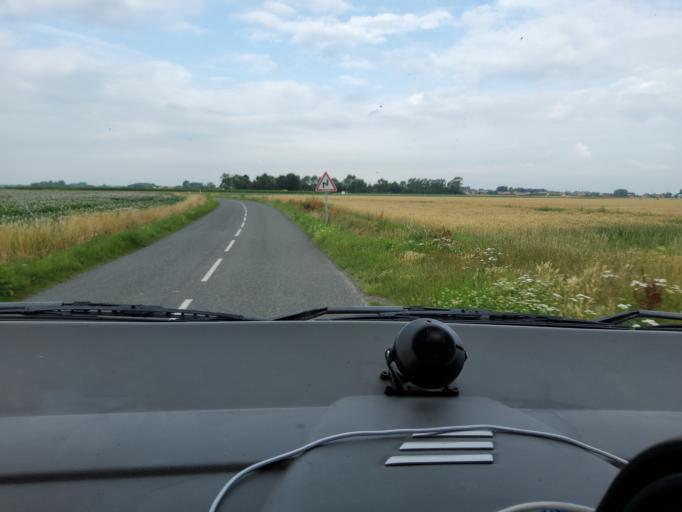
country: FR
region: Nord-Pas-de-Calais
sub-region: Departement du Nord
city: Brouckerque
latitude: 50.9548
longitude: 2.3108
